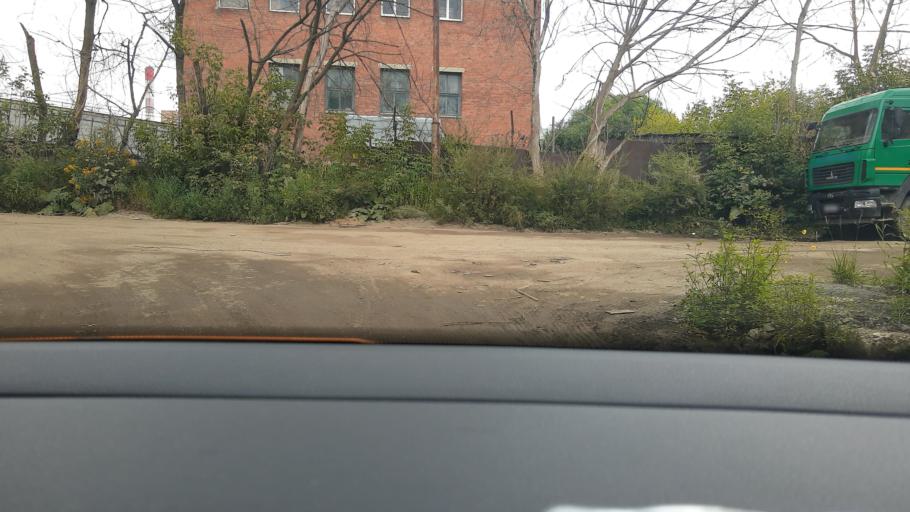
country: RU
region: Moscow
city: Metrogorodok
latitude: 55.8108
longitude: 37.7532
